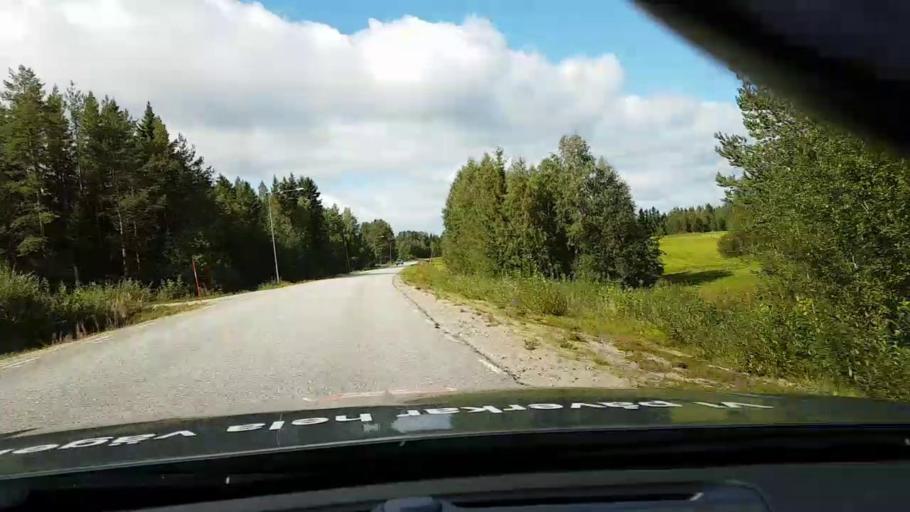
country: SE
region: Vaesterbotten
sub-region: Asele Kommun
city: Asele
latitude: 63.9332
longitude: 17.2916
